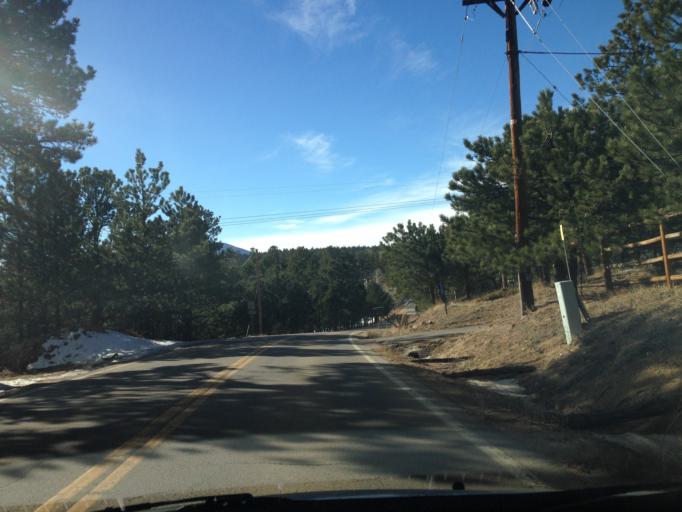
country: US
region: Colorado
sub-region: Boulder County
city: Boulder
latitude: 39.9825
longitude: -105.3249
